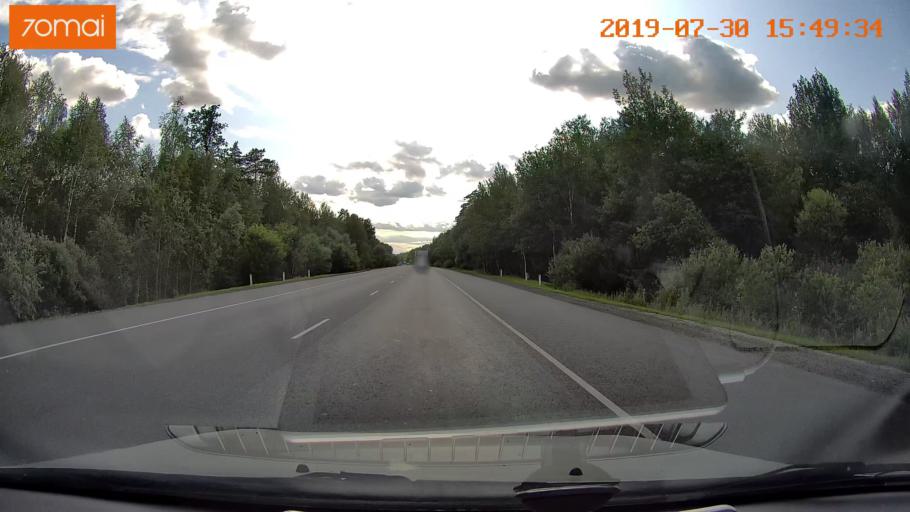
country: RU
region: Moskovskaya
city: Voskresensk
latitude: 55.3369
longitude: 38.6652
